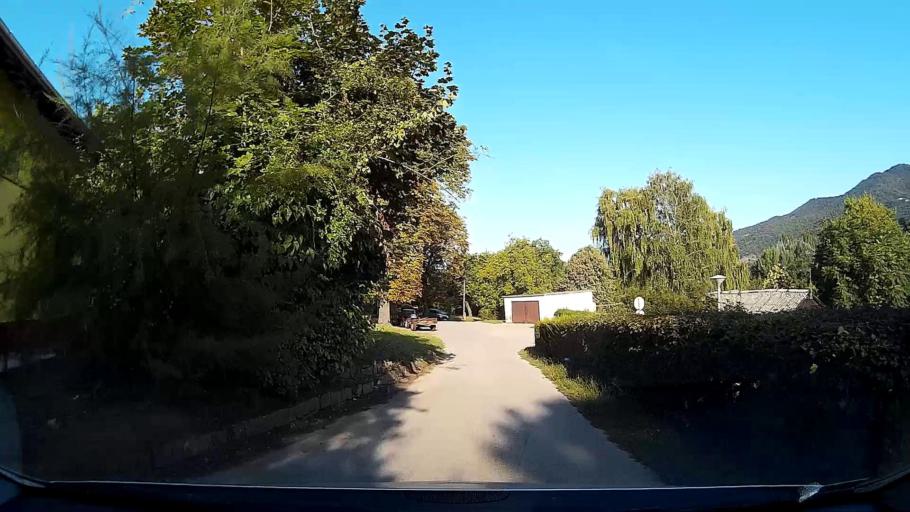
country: HU
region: Pest
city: Nagymaros
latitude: 47.7590
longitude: 18.9405
